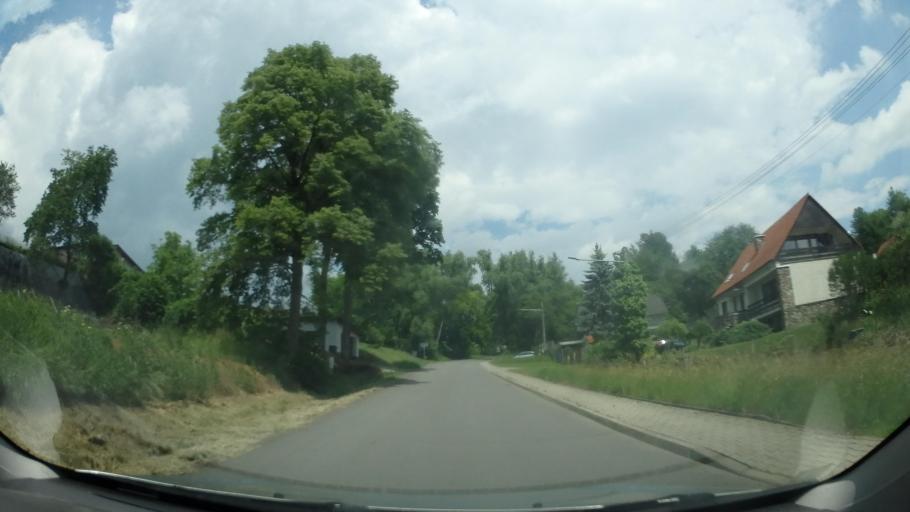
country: CZ
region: South Moravian
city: Boritov
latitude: 49.4283
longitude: 16.5912
